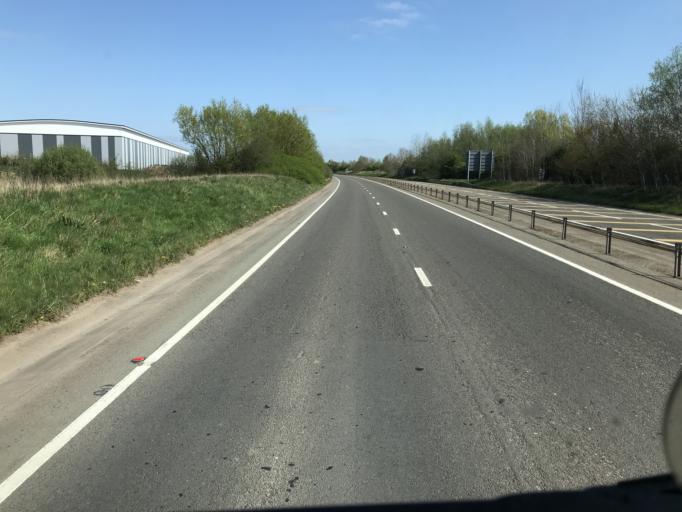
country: GB
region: England
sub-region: Cheshire East
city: Crewe
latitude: 53.0707
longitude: -2.4362
